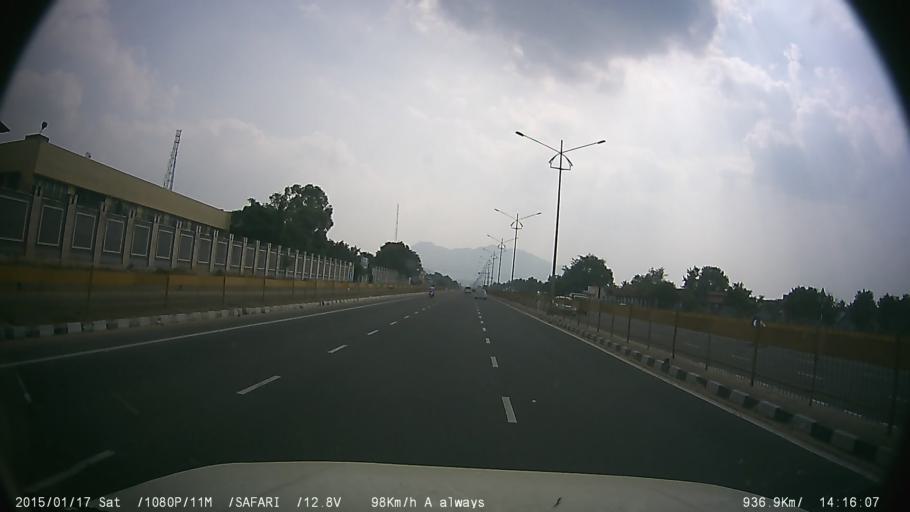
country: IN
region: Tamil Nadu
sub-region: Vellore
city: Ambur
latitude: 12.7595
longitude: 78.7007
